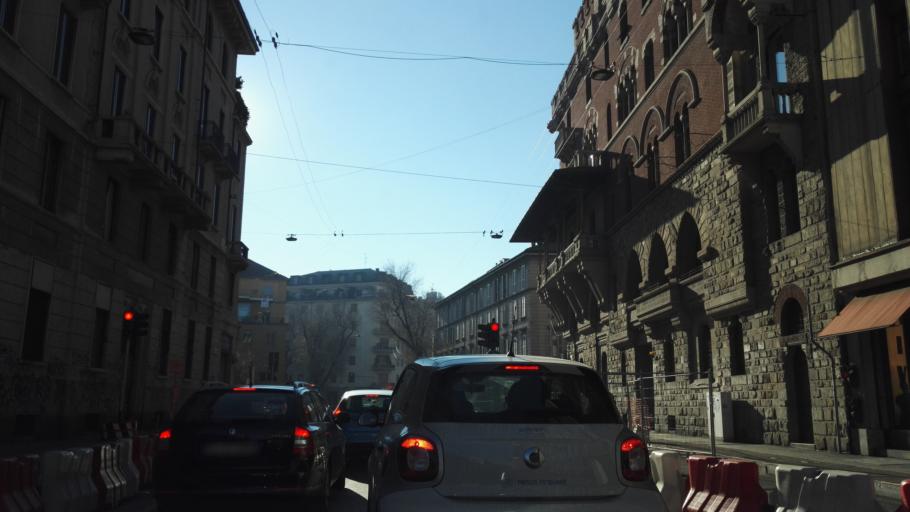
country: IT
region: Lombardy
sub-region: Citta metropolitana di Milano
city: Milano
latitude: 45.4628
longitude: 9.1739
